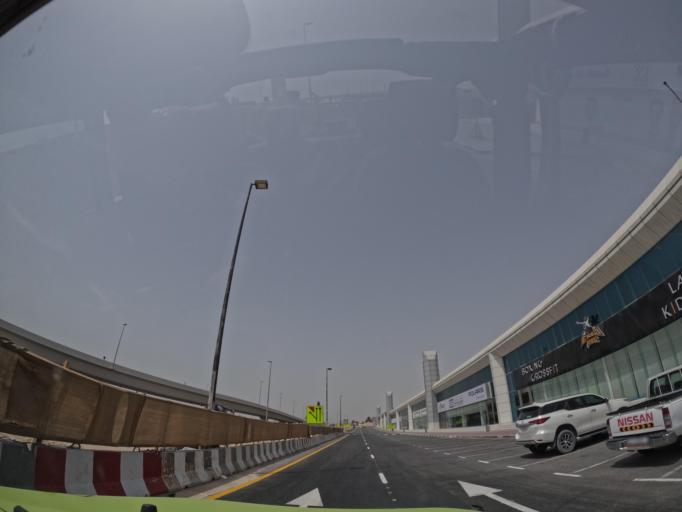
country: AE
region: Ash Shariqah
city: Sharjah
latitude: 25.1866
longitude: 55.3717
